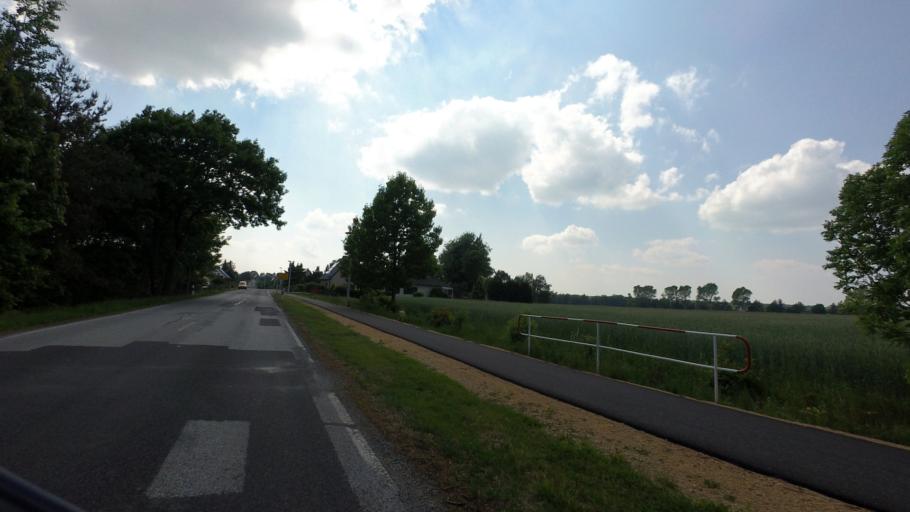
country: DE
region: Saxony
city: Mucka
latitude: 51.3018
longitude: 14.6690
